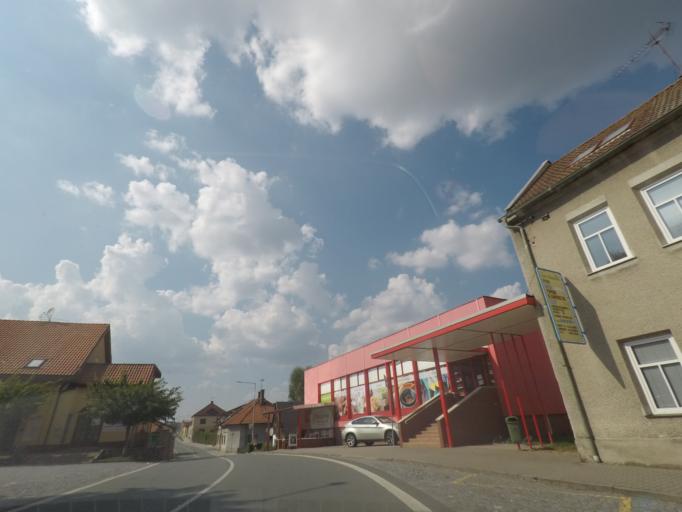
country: CZ
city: Borohradek
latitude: 50.0977
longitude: 16.0935
